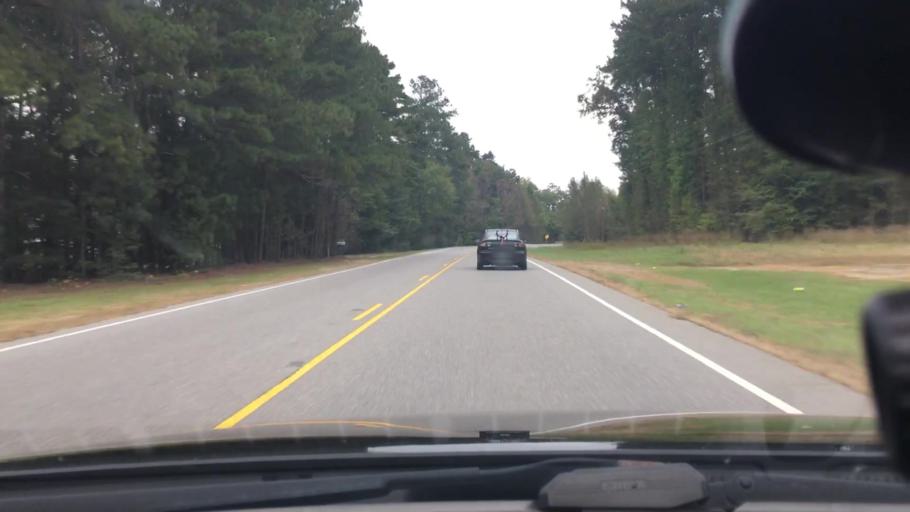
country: US
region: North Carolina
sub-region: Moore County
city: Robbins
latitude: 35.3876
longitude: -79.6513
